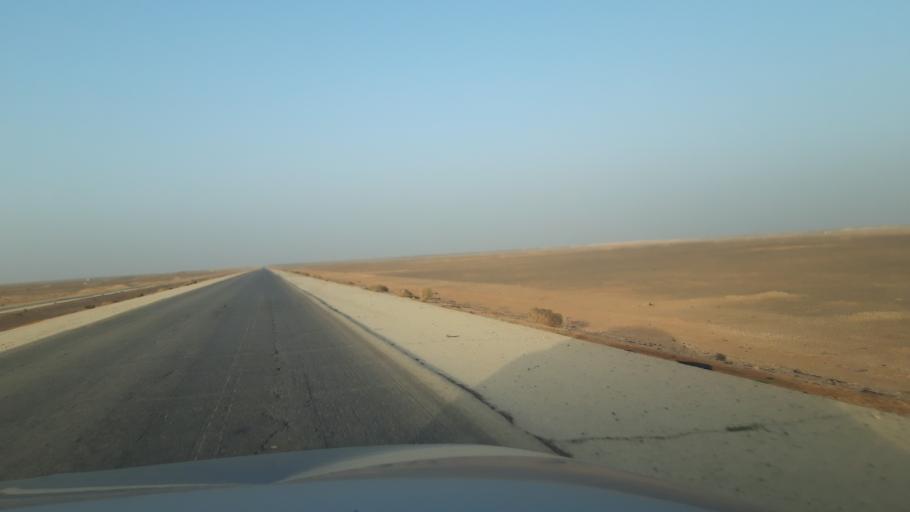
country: JO
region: Ma'an
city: Al Jafr
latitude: 30.2092
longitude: 36.0973
